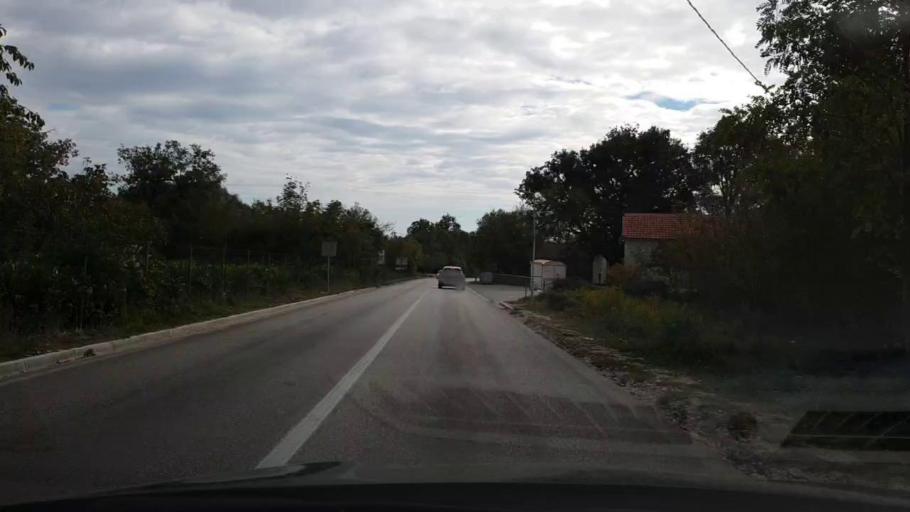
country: ME
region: Herceg Novi
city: Herceg-Novi
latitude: 42.4801
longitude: 18.5292
